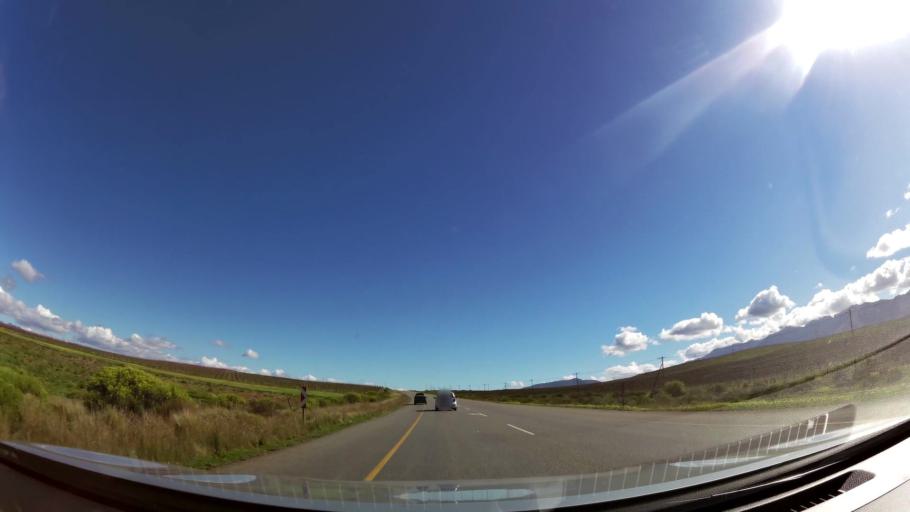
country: ZA
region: Western Cape
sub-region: Cape Winelands District Municipality
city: Ashton
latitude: -33.8184
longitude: 19.9664
